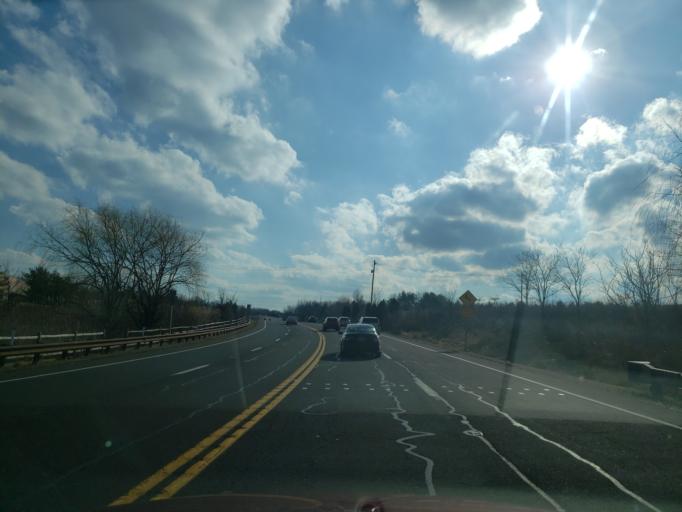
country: US
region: Pennsylvania
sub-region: Montgomery County
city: Montgomeryville
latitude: 40.2288
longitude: -75.2417
